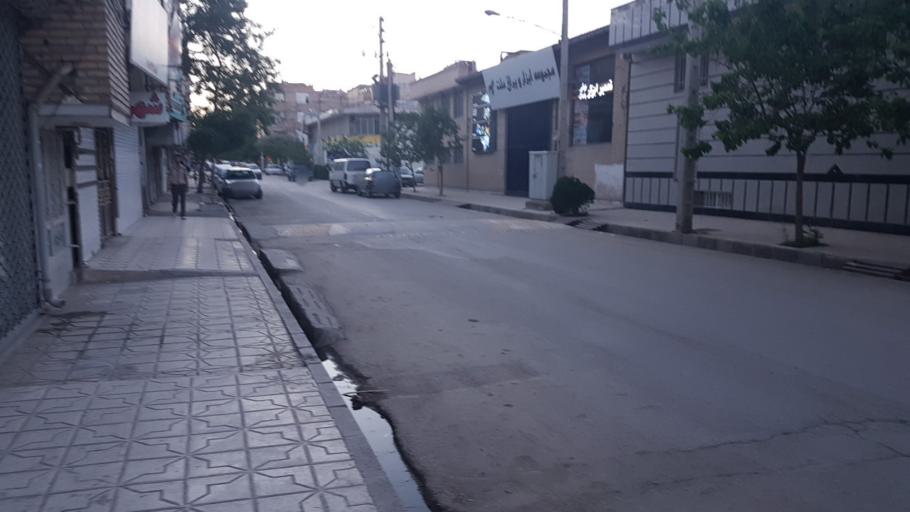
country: IR
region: Razavi Khorasan
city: Mashhad
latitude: 36.3518
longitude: 59.5776
